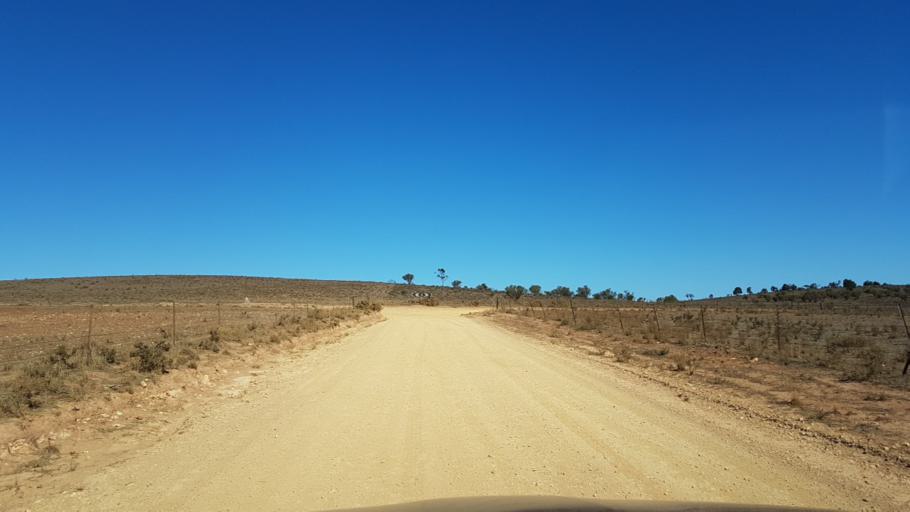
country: AU
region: South Australia
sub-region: Peterborough
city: Peterborough
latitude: -32.9917
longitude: 138.8318
